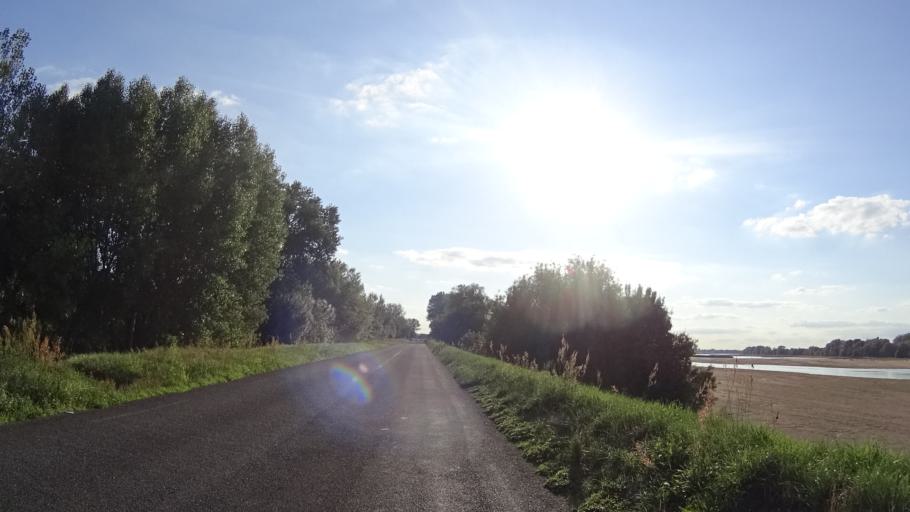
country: FR
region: Pays de la Loire
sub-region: Departement de Maine-et-Loire
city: Le Mesnil-en-Vallee
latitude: 47.3783
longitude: -0.9481
